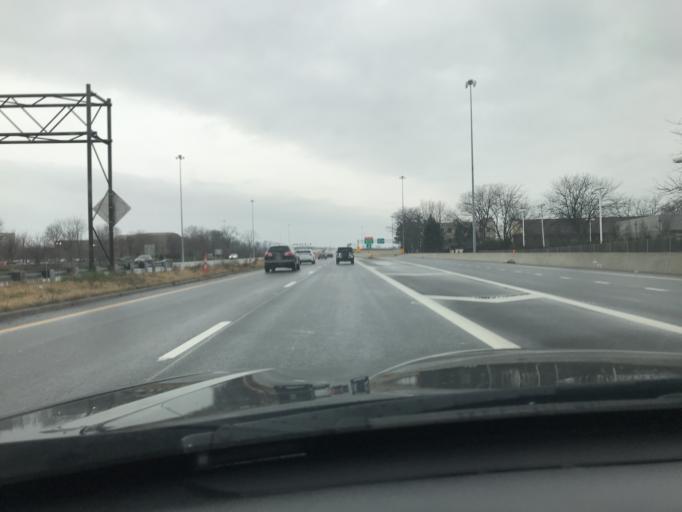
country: US
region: Ohio
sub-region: Franklin County
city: Dublin
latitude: 40.0993
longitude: -83.1264
